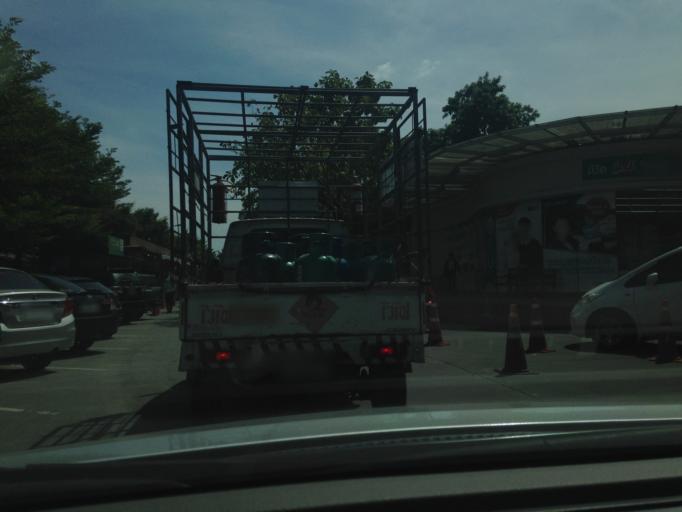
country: TH
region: Bangkok
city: Lat Krabang
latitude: 13.7214
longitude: 100.7275
